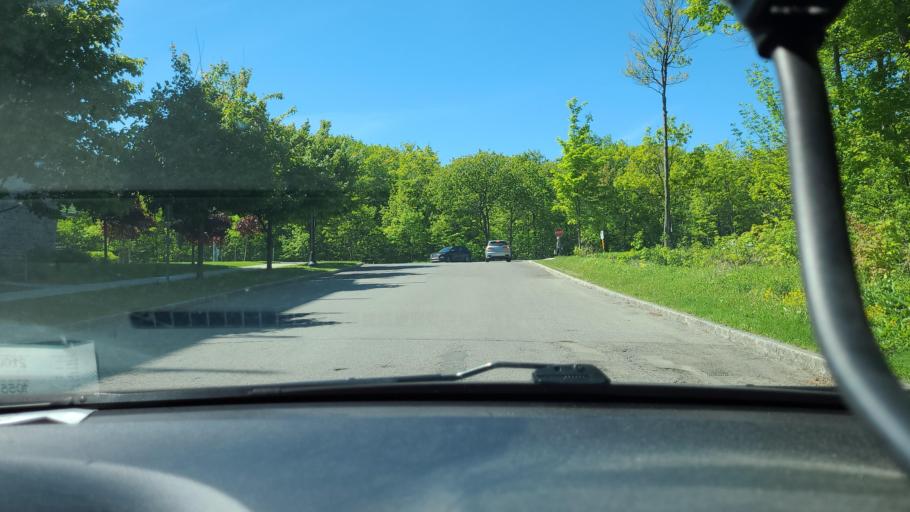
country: CA
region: Quebec
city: L'Ancienne-Lorette
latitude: 46.7561
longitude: -71.3263
